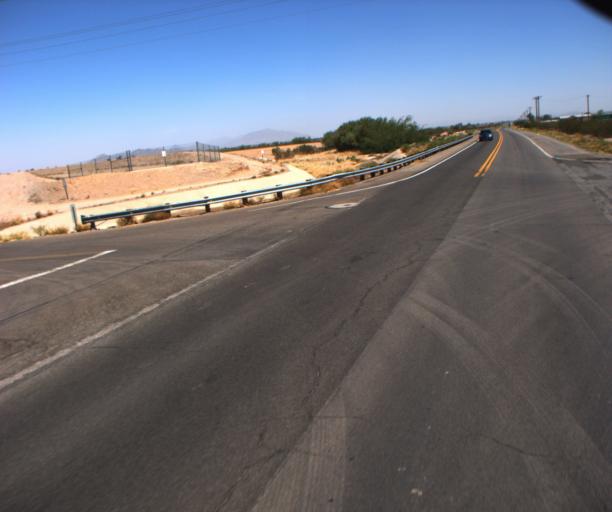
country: US
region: Arizona
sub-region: Pinal County
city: Maricopa
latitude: 32.8791
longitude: -112.0492
